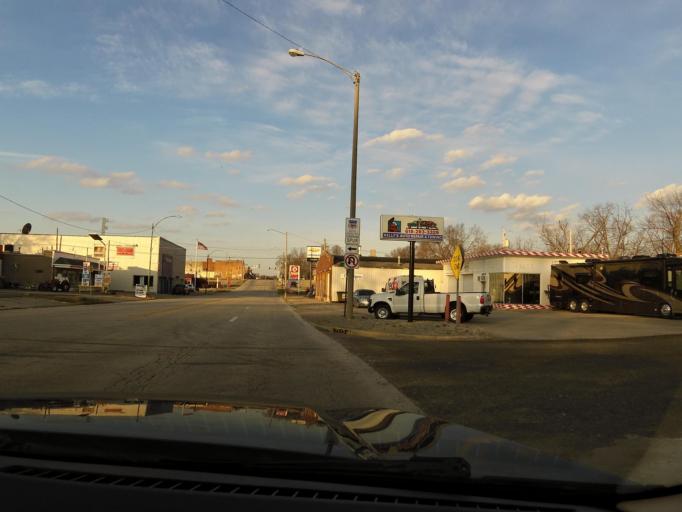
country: US
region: Illinois
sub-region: Fayette County
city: Vandalia
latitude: 38.9607
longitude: -89.0903
